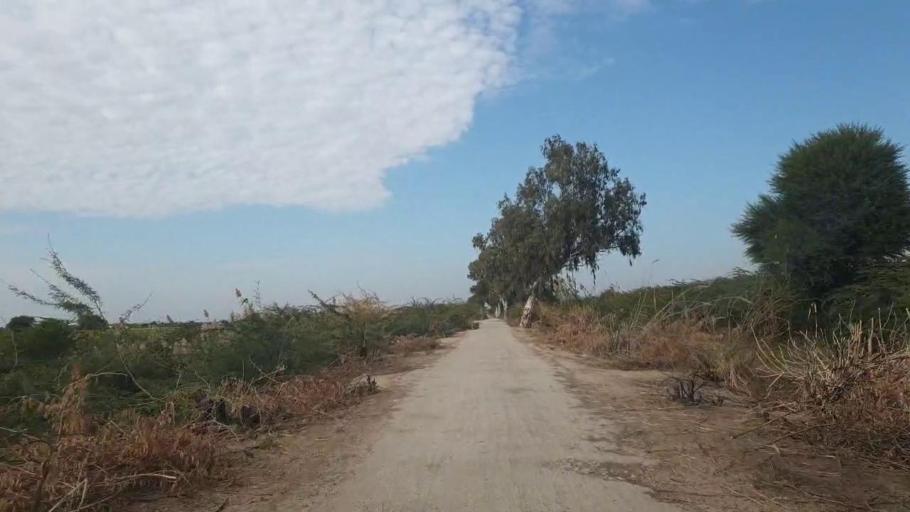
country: PK
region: Sindh
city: Sinjhoro
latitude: 26.0455
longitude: 68.8765
